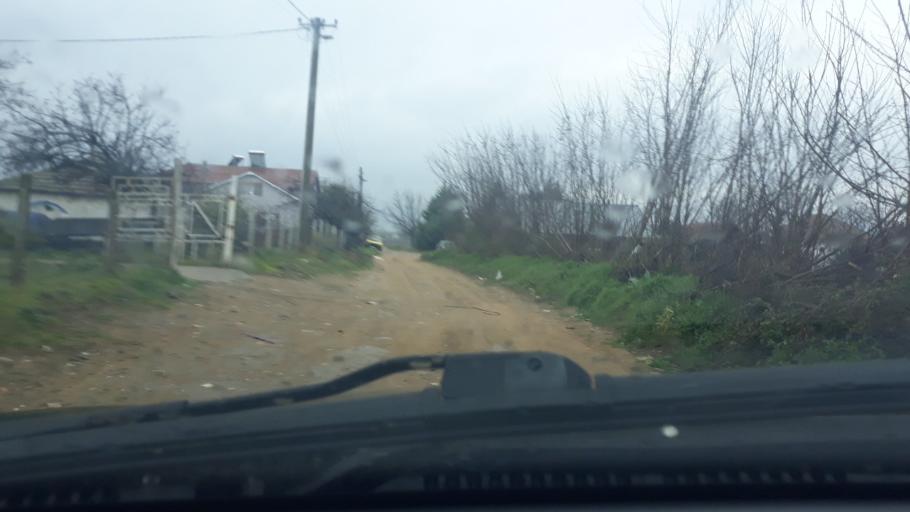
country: MK
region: Gevgelija
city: Miravci
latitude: 41.3295
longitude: 22.4799
